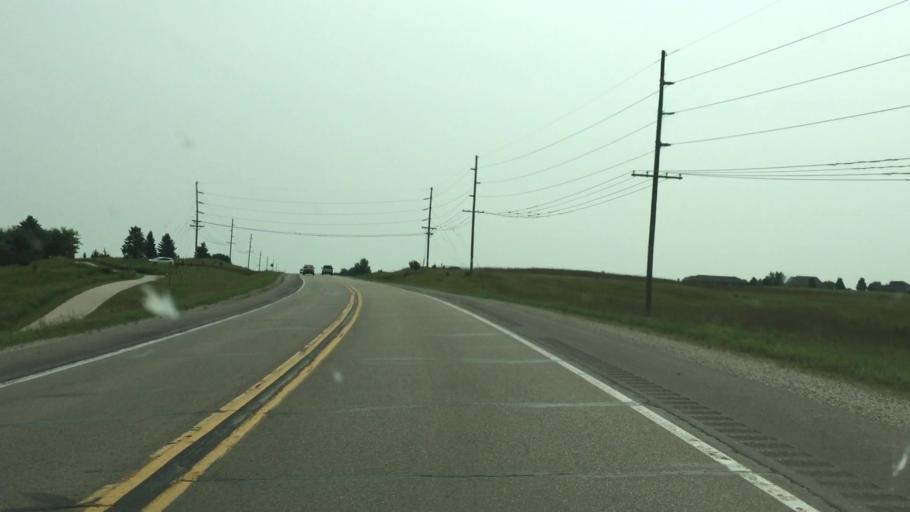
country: US
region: Iowa
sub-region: Dickinson County
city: Milford
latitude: 43.3424
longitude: -95.1743
